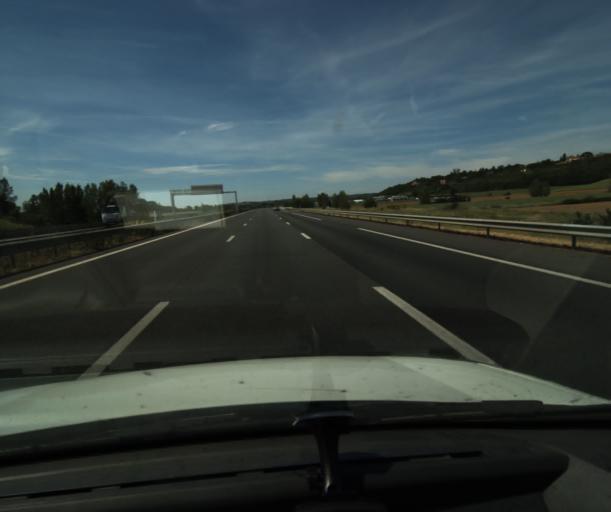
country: FR
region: Midi-Pyrenees
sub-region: Departement de la Haute-Garonne
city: Saint-Sauveur
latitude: 43.7386
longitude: 1.3931
